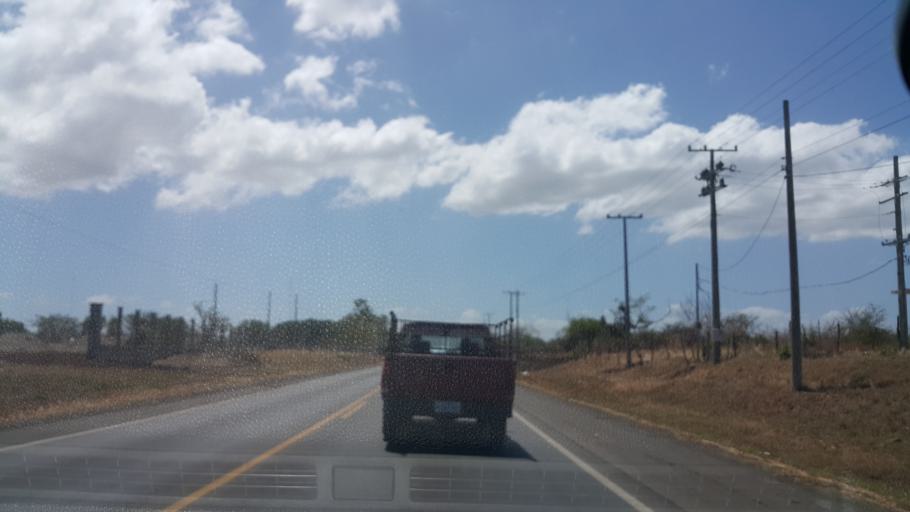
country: NI
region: Managua
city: Tipitapa
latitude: 12.2423
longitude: -86.0906
